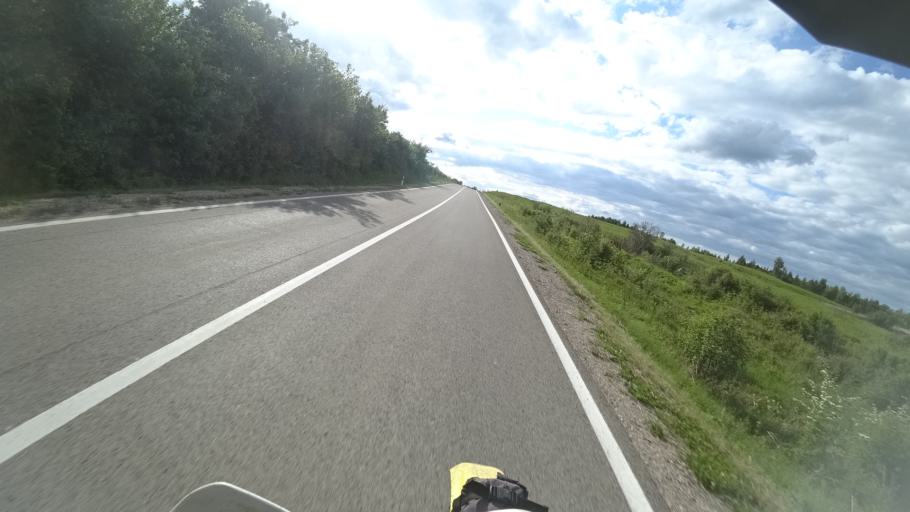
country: HR
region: Licko-Senjska
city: Gospic
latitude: 44.5022
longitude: 15.4501
